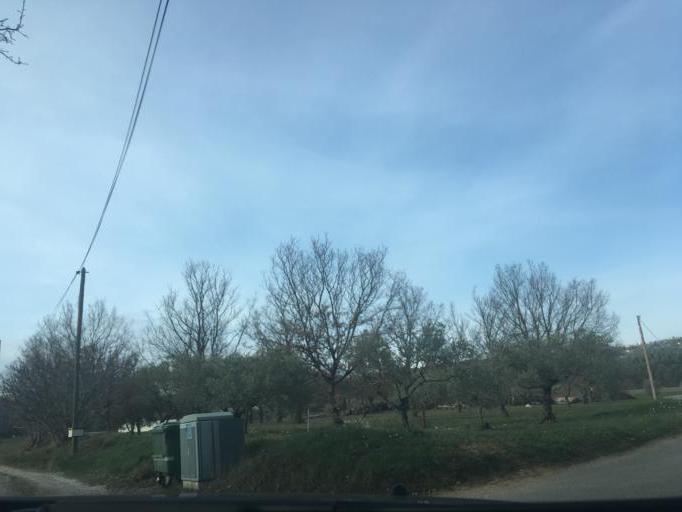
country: FR
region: Provence-Alpes-Cote d'Azur
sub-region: Departement du Var
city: Villecroze
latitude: 43.5618
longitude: 6.2813
